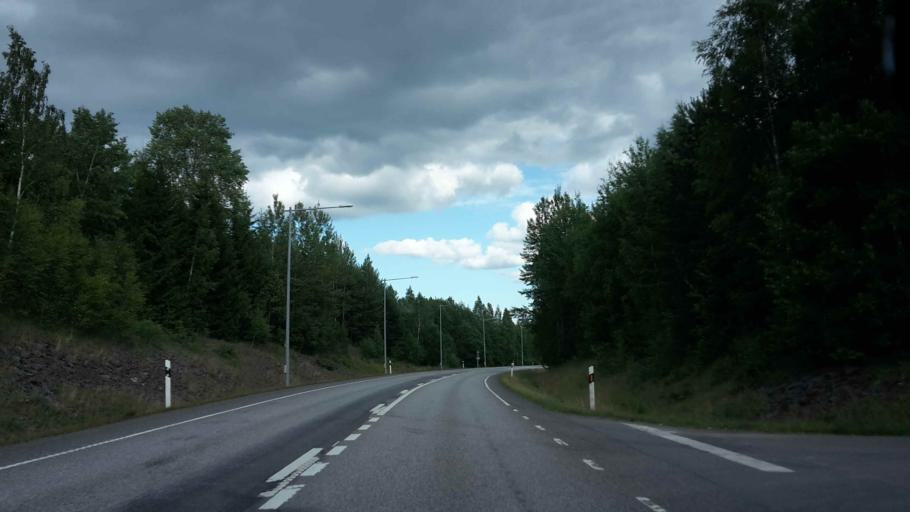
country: SE
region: OEstergoetland
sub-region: Linkopings Kommun
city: Ljungsbro
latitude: 58.7907
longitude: 15.4782
